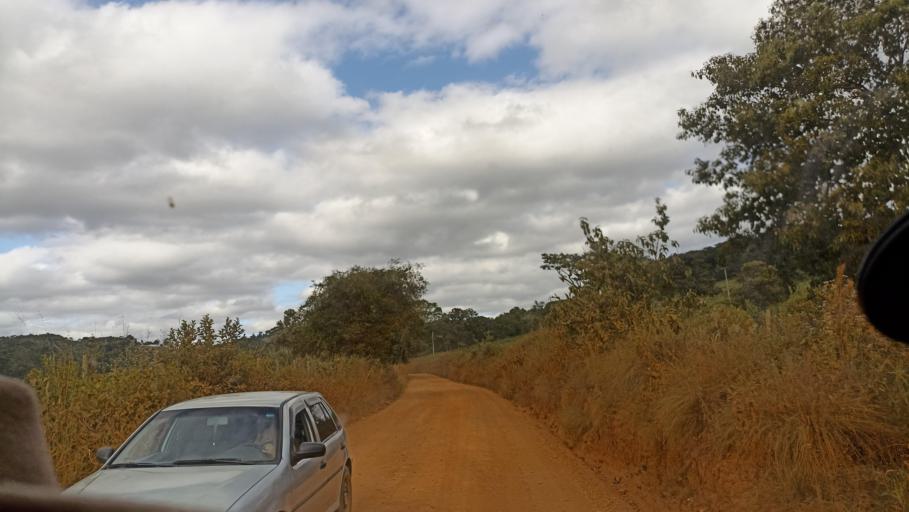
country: BR
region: Minas Gerais
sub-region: Tiradentes
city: Tiradentes
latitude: -21.1023
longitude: -44.1059
